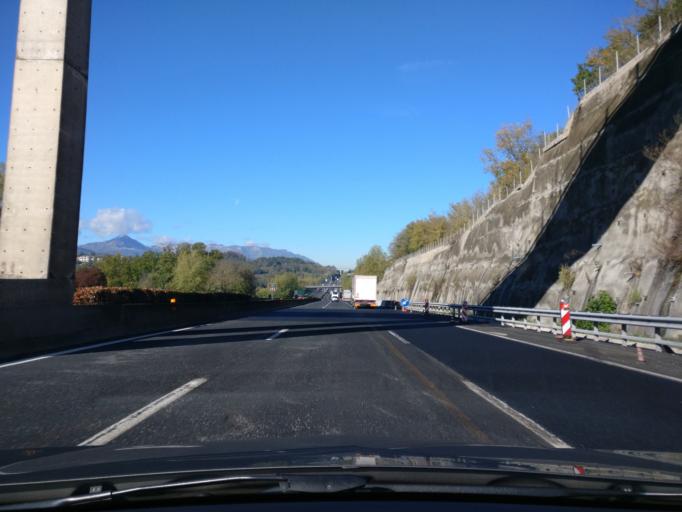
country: IT
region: Latium
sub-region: Provincia di Frosinone
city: Arnara
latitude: 41.5738
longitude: 13.3753
